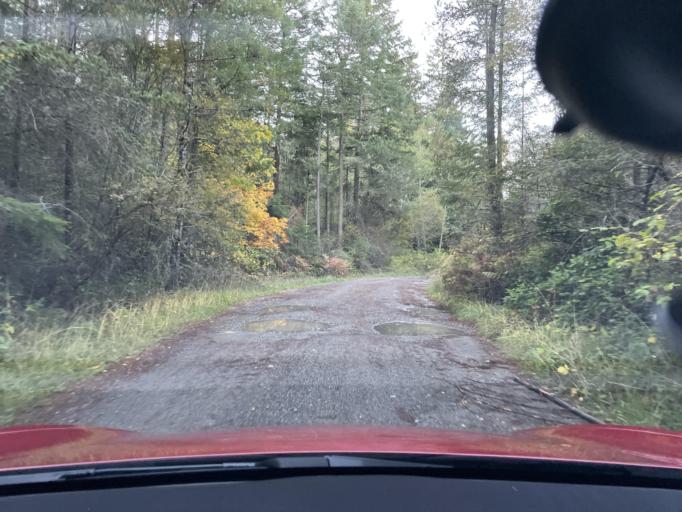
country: US
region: Washington
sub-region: San Juan County
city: Friday Harbor
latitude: 48.6155
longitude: -123.1393
